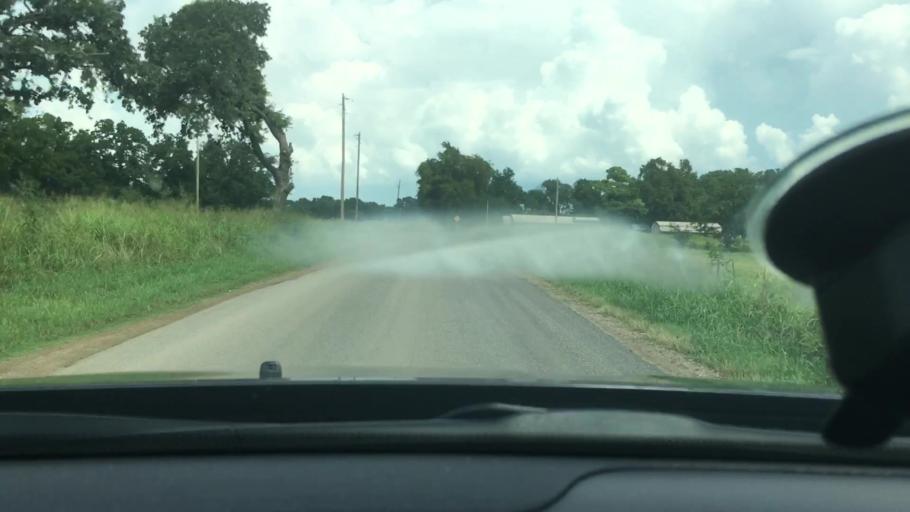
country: US
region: Oklahoma
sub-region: Carter County
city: Dickson
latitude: 34.2008
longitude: -96.8982
